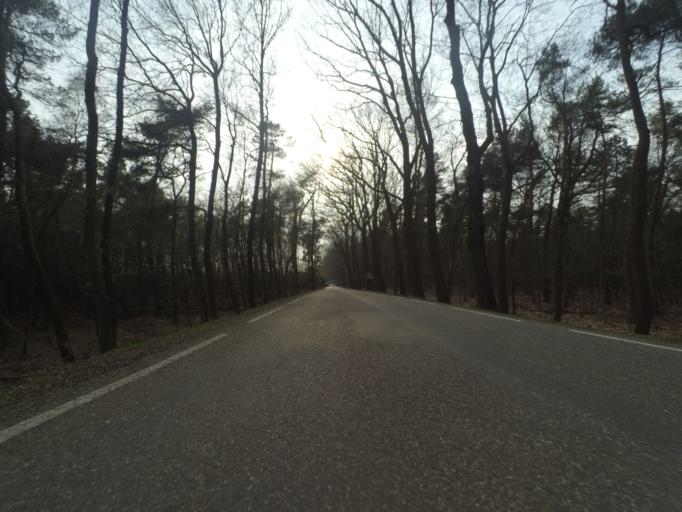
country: NL
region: Gelderland
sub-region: Gemeente Apeldoorn
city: Beekbergen
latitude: 52.1295
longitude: 5.9076
